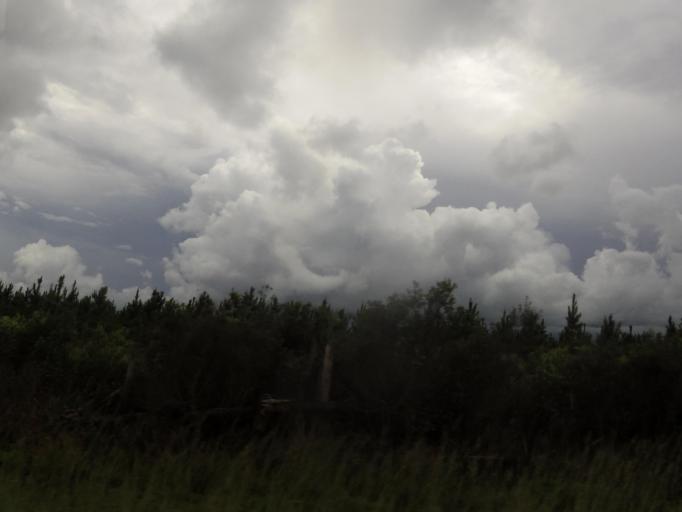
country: US
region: Florida
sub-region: Baker County
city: Macclenny
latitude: 30.5174
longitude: -82.1041
